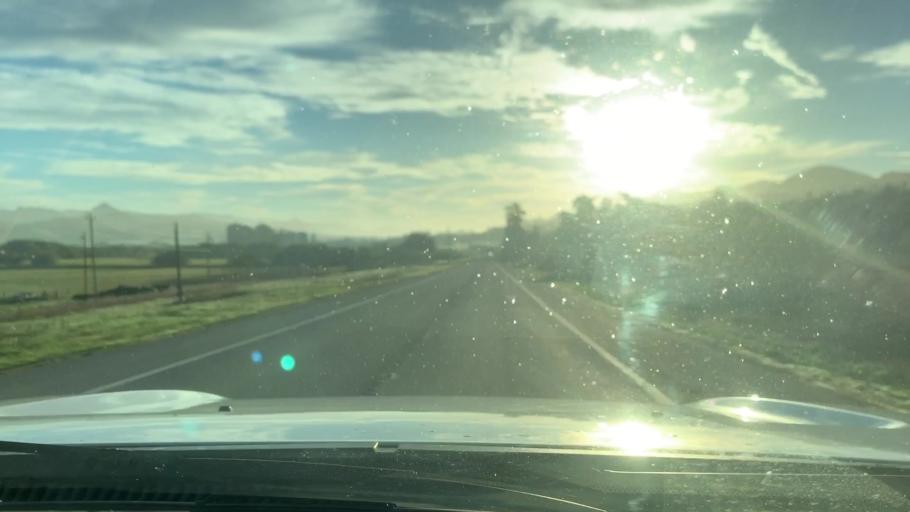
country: US
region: California
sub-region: San Luis Obispo County
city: Los Osos
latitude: 35.3008
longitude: -120.7909
